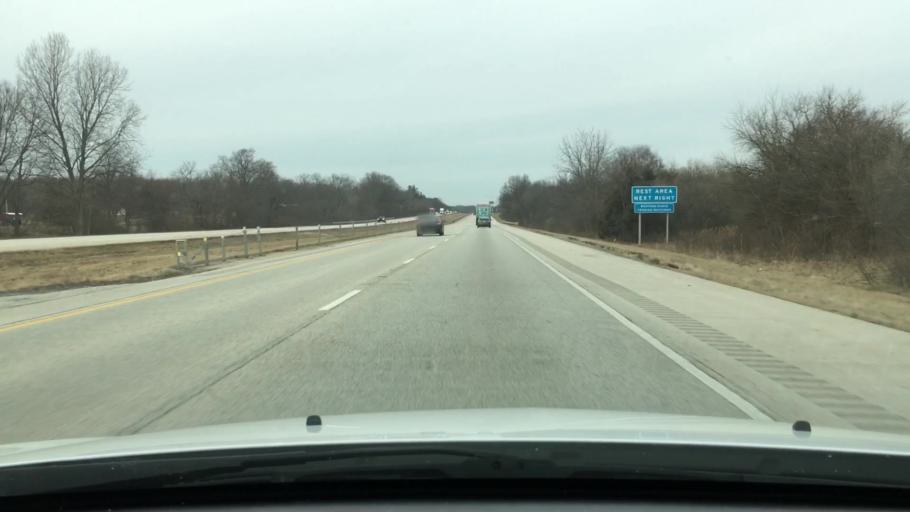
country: US
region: Illinois
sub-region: Sangamon County
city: Sherman
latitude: 39.8554
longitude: -89.5949
